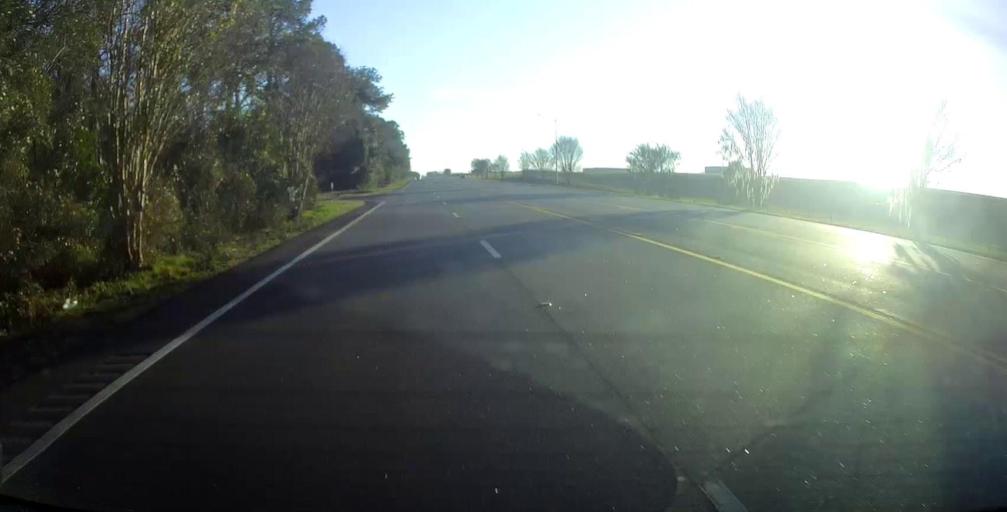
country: US
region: Georgia
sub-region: Dougherty County
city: Albany
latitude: 31.5391
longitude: -84.1819
